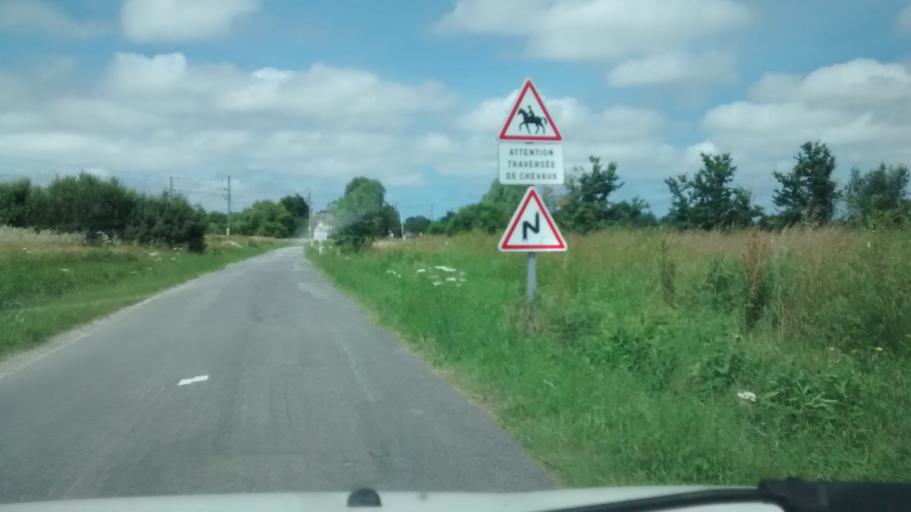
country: FR
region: Brittany
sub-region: Departement d'Ille-et-Vilaine
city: La Gouesniere
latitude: 48.6107
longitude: -1.8811
